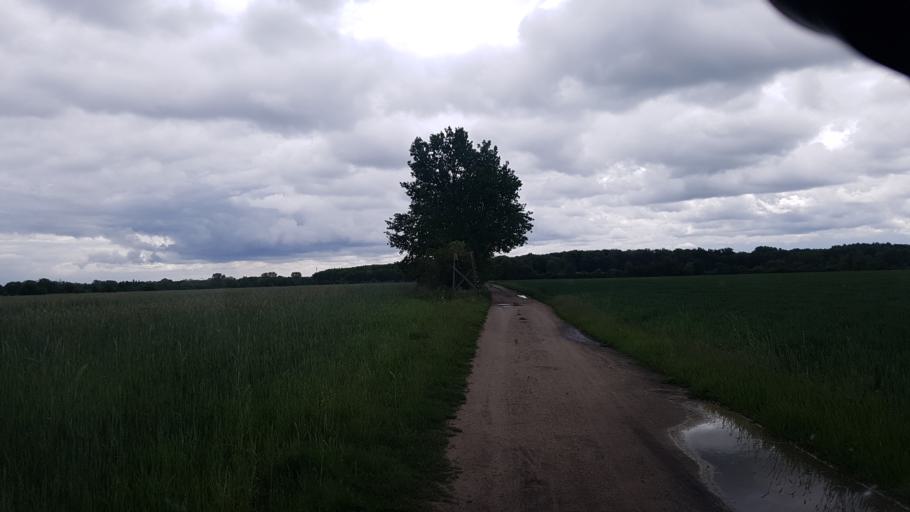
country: DE
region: Brandenburg
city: Doberlug-Kirchhain
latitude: 51.6297
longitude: 13.5398
